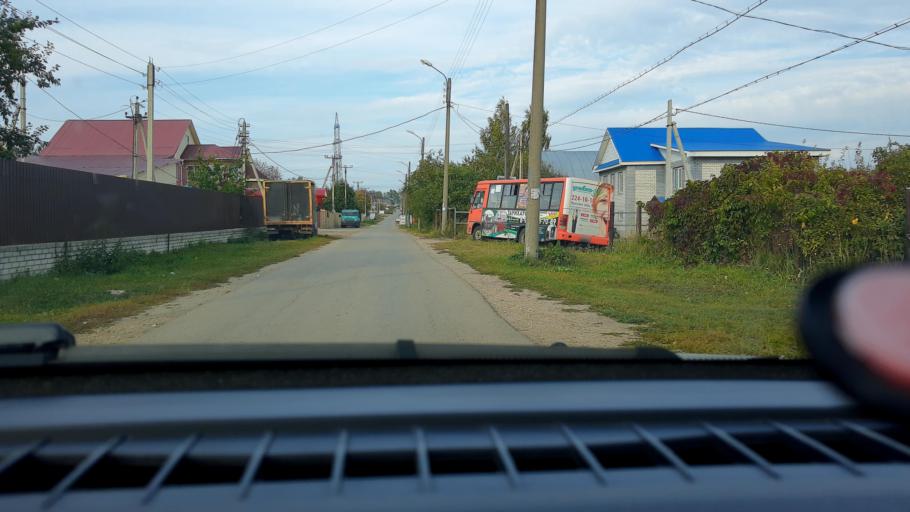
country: RU
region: Nizjnij Novgorod
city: Nizhniy Novgorod
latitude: 56.2089
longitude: 43.9545
